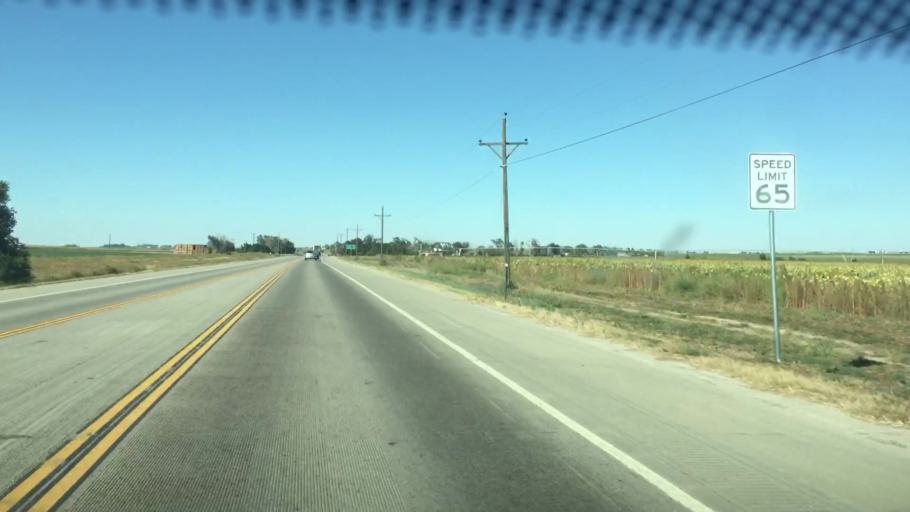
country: US
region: Colorado
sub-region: Prowers County
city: Lamar
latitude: 38.1607
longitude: -102.7238
